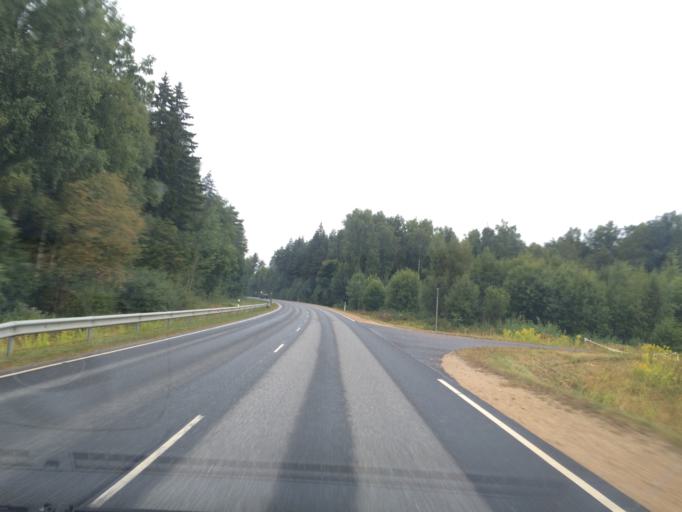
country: LV
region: Ogre
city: Ogre
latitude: 56.8585
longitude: 24.5888
